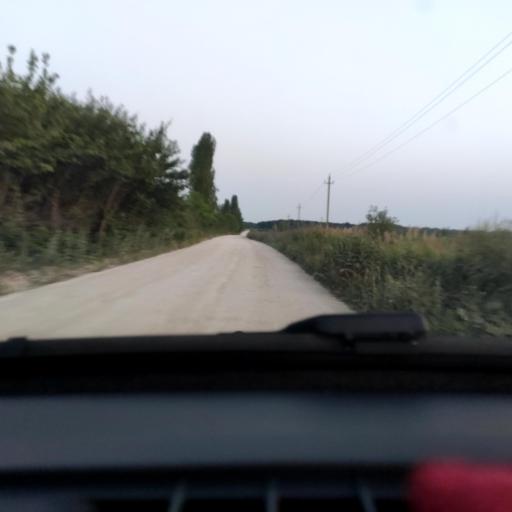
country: RU
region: Voronezj
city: Podgornoye
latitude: 51.8627
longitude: 39.1018
